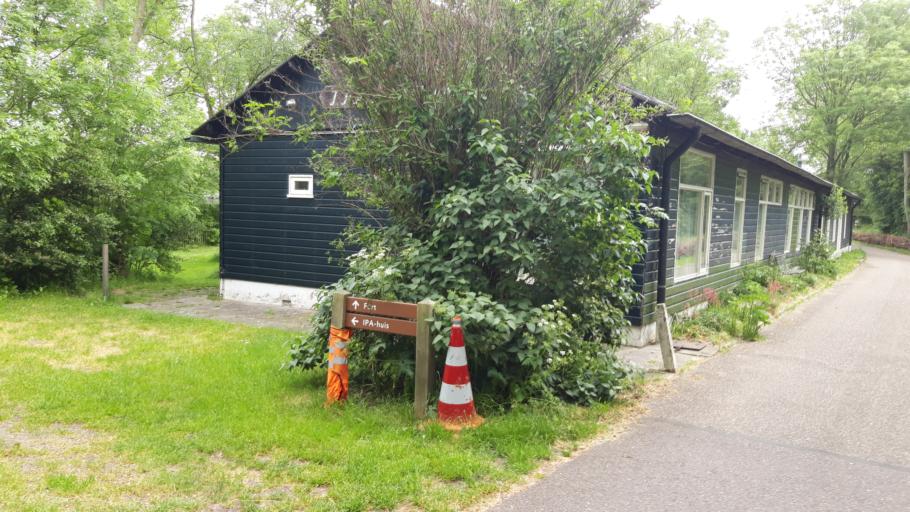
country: NL
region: North Holland
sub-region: Gemeente Beemster
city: Halfweg
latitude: 52.5399
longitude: 4.8397
